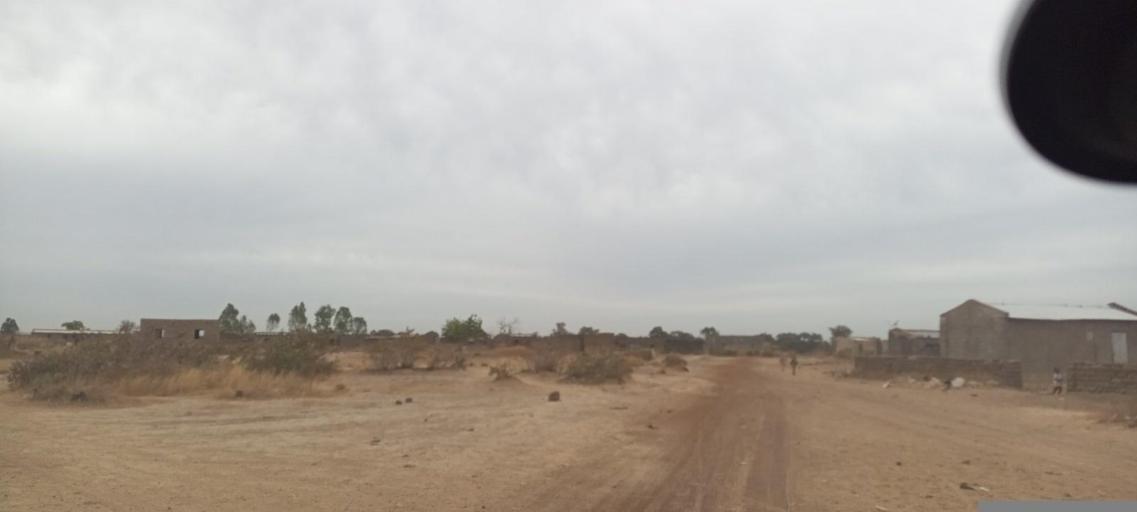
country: ML
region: Koulikoro
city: Kati
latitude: 12.7973
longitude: -8.2497
